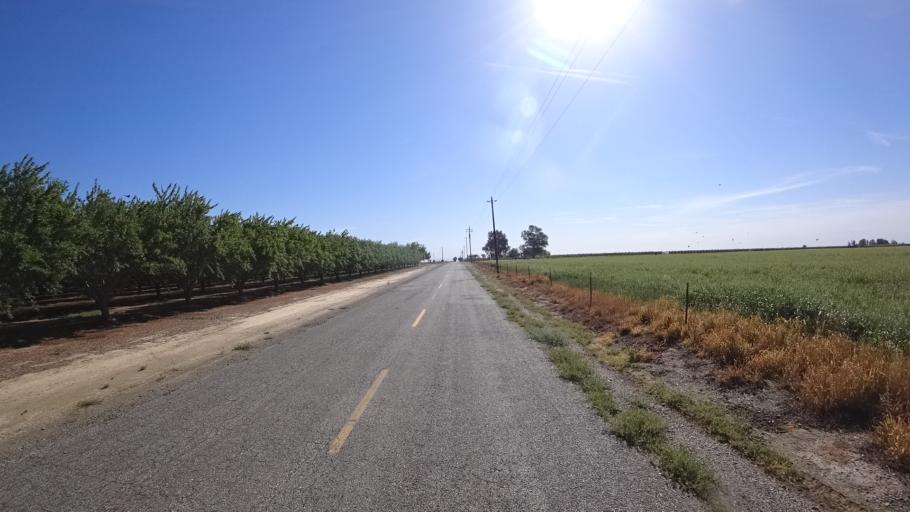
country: US
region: California
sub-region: Glenn County
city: Willows
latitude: 39.6113
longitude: -122.1603
